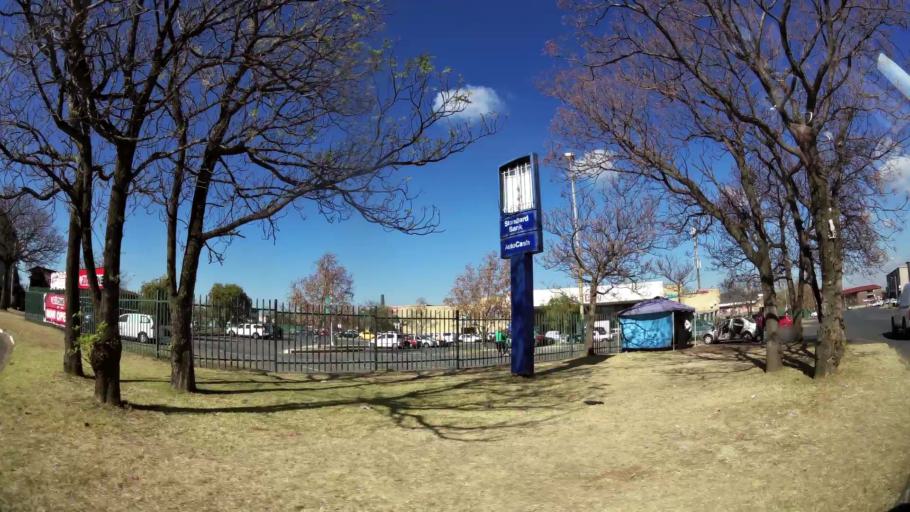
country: ZA
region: Gauteng
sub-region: City of Johannesburg Metropolitan Municipality
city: Roodepoort
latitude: -26.1402
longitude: 27.8320
